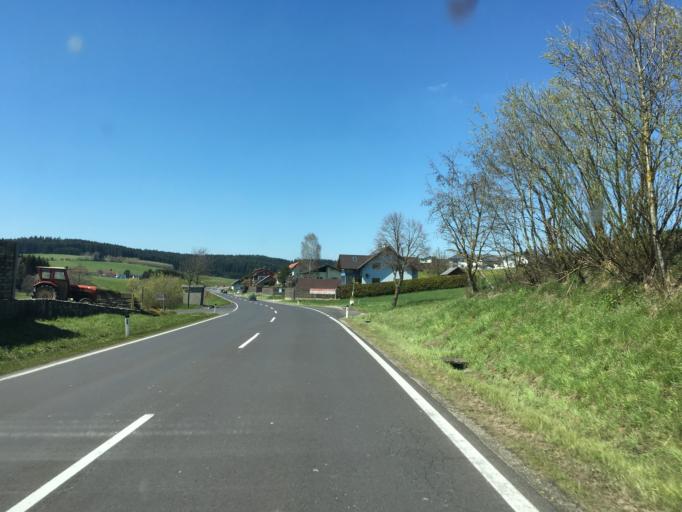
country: AT
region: Upper Austria
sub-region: Politischer Bezirk Urfahr-Umgebung
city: Bad Leonfelden
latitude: 48.4992
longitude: 14.3004
